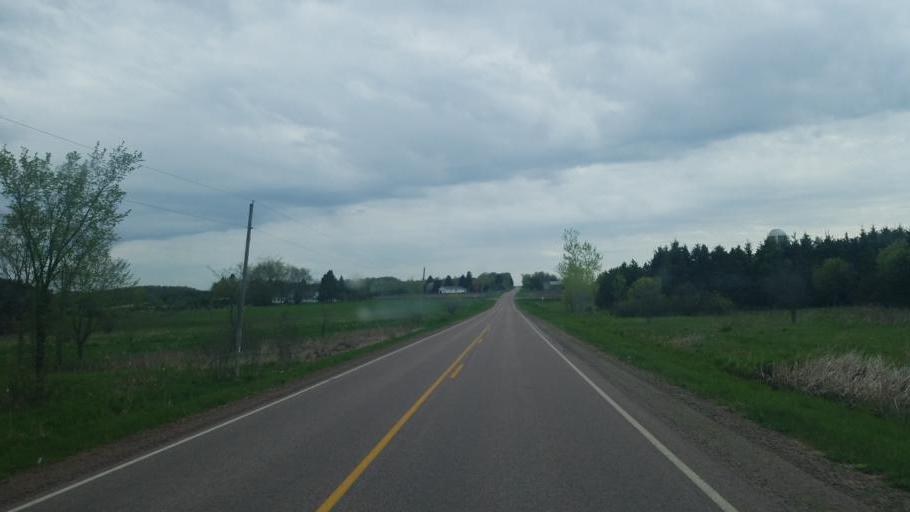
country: US
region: Wisconsin
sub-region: Wood County
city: Marshfield
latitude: 44.5814
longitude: -90.2995
